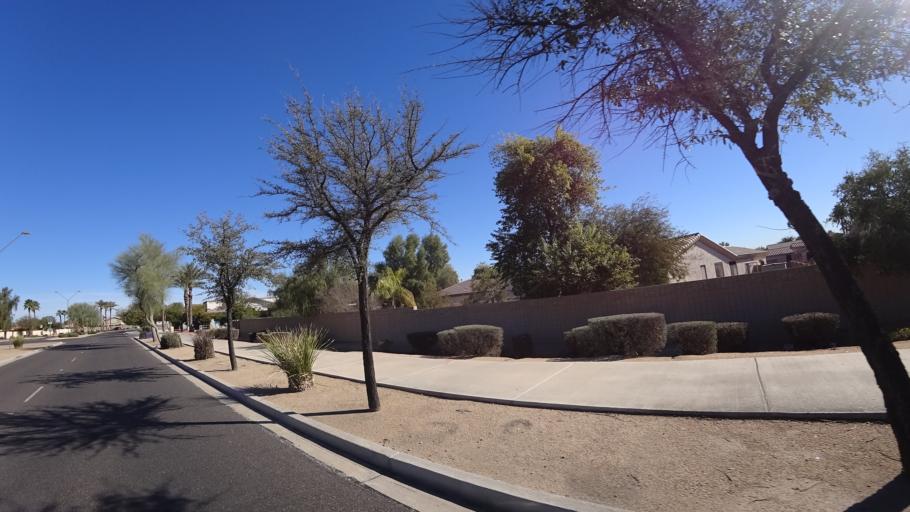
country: US
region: Arizona
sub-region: Maricopa County
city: Litchfield Park
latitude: 33.4845
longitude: -112.3740
